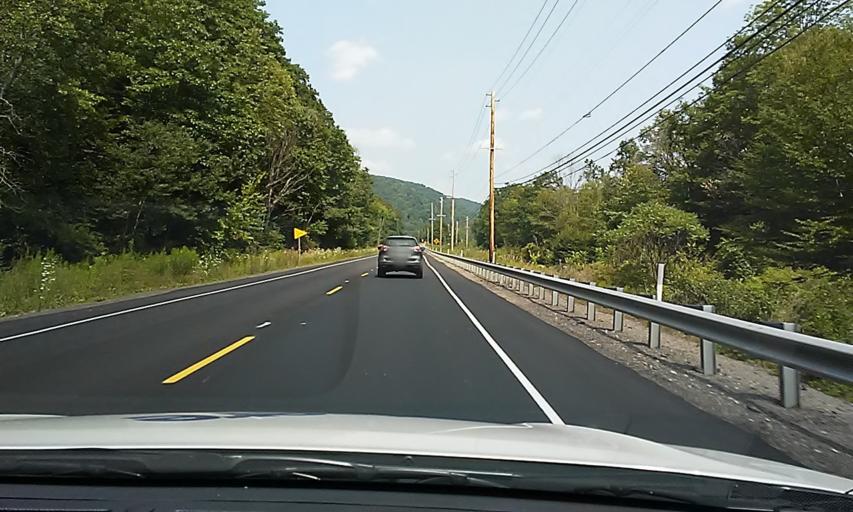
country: US
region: Pennsylvania
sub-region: Cameron County
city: Emporium
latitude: 41.4757
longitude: -78.3272
